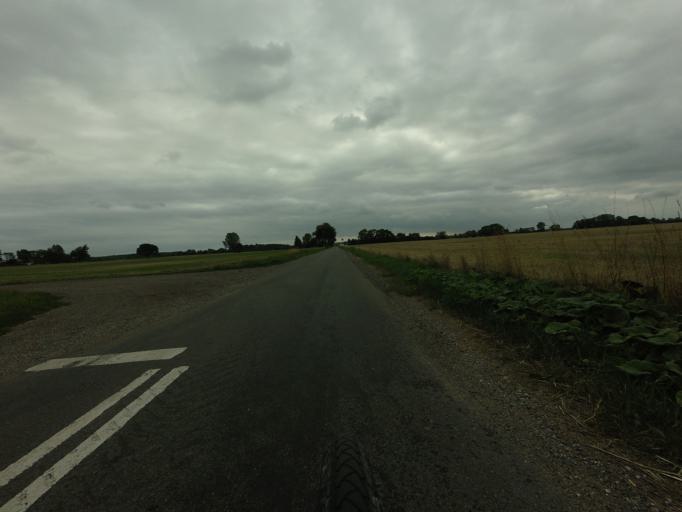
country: DK
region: Zealand
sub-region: Stevns Kommune
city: Store Heddinge
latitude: 55.3409
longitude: 12.3350
